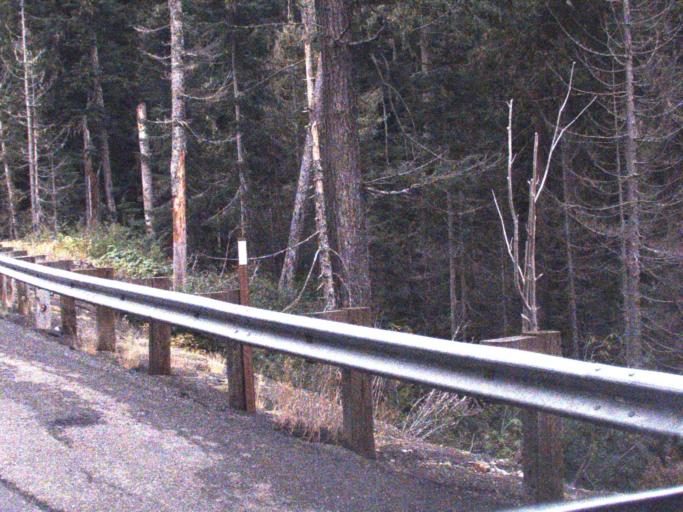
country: US
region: Washington
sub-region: Yakima County
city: Tieton
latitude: 46.6274
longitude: -121.4261
